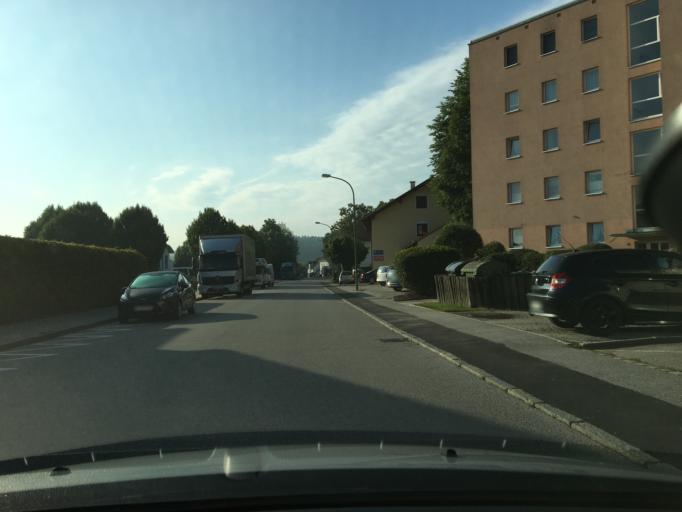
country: DE
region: Bavaria
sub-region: Lower Bavaria
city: Vilsbiburg
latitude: 48.4578
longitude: 12.3599
